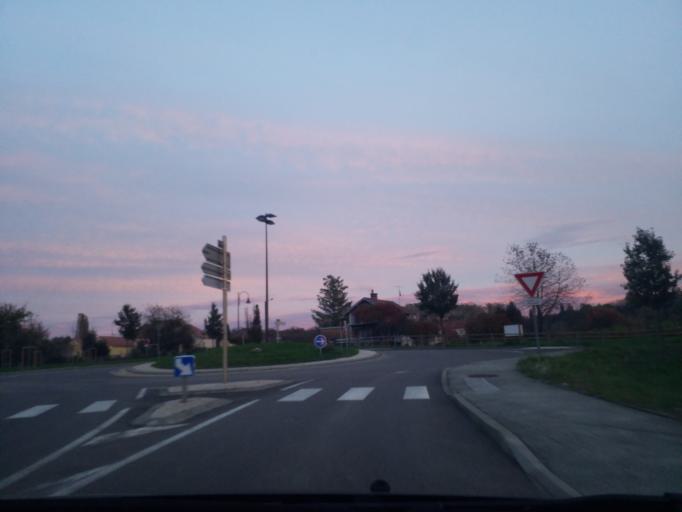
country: FR
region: Franche-Comte
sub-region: Departement de la Haute-Saone
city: Villersexel
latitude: 47.5566
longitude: 6.4311
